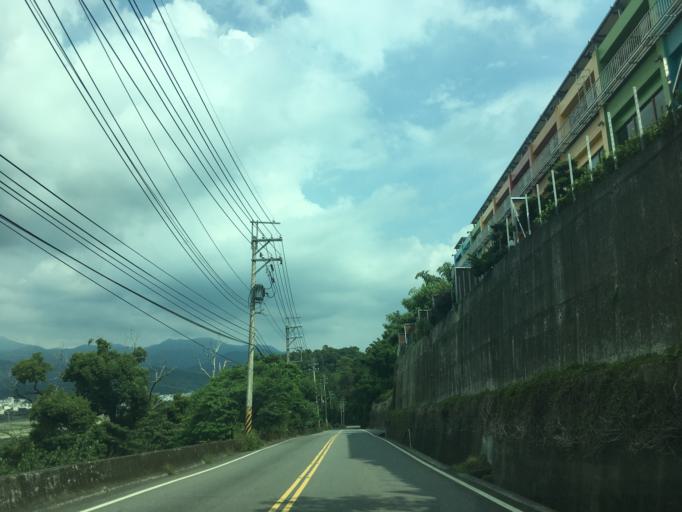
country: TW
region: Taiwan
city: Fengyuan
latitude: 24.2566
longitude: 120.8093
